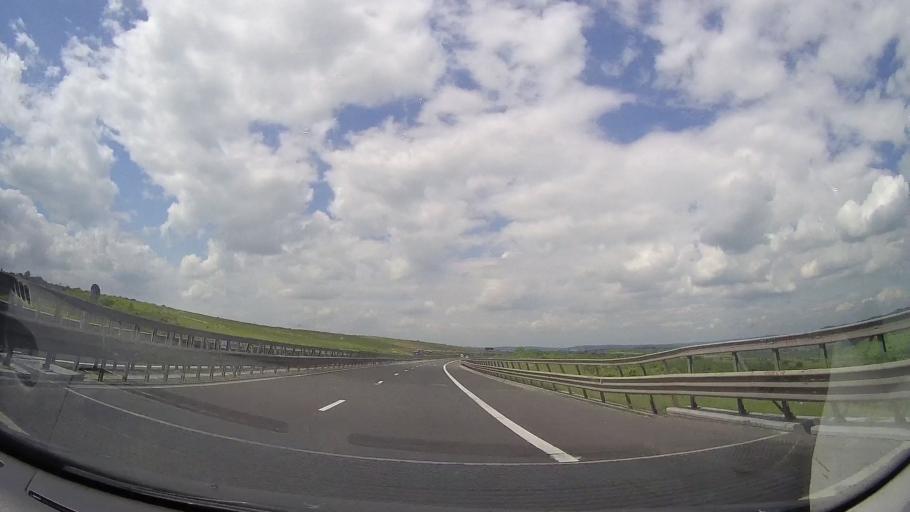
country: RO
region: Sibiu
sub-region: Comuna Tilisca
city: Tilisca
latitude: 45.8291
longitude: 23.8634
